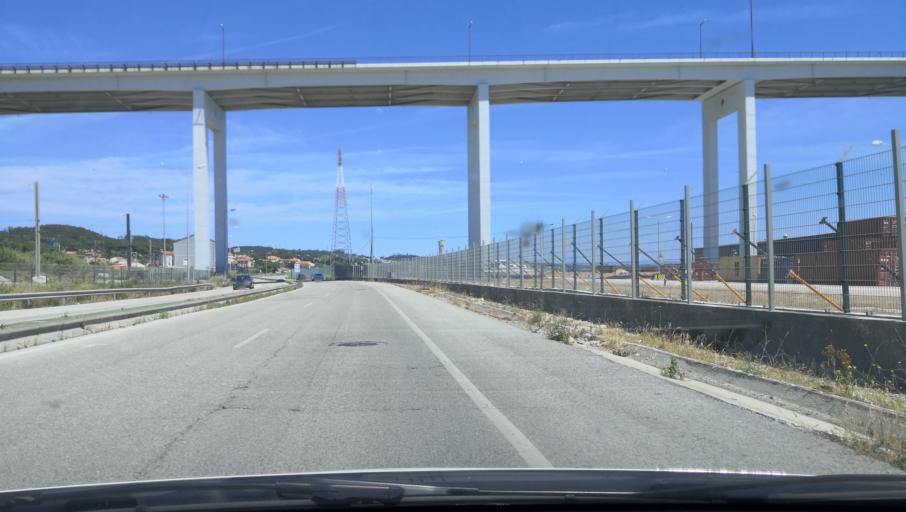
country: PT
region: Coimbra
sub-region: Figueira da Foz
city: Figueira da Foz
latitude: 40.1479
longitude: -8.8433
